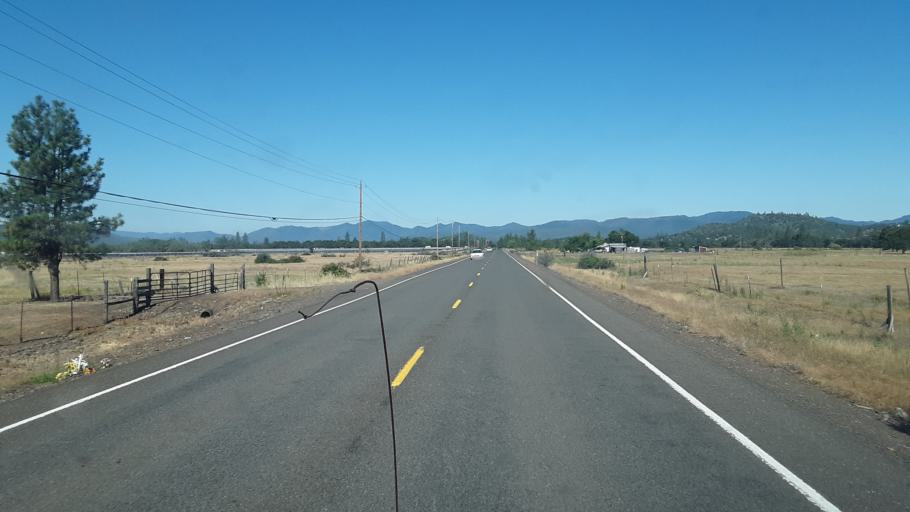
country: US
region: Oregon
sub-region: Jackson County
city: Eagle Point
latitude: 42.5237
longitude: -122.8209
